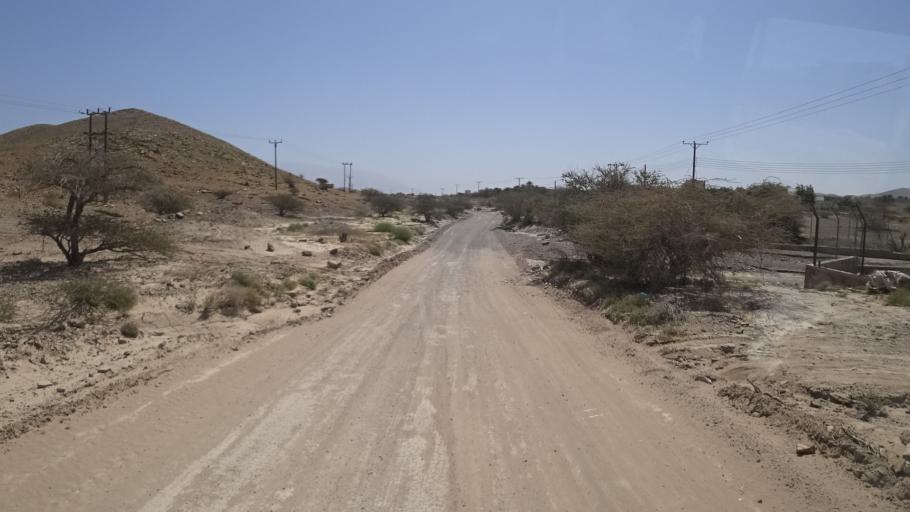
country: OM
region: Az Zahirah
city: `Ibri
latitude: 23.2655
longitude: 56.7466
